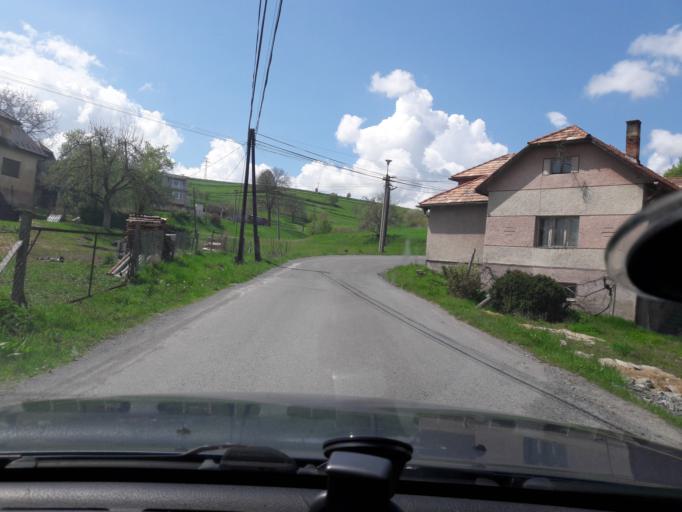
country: SK
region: Banskobystricky
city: Hrinova
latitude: 48.5783
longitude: 19.4941
